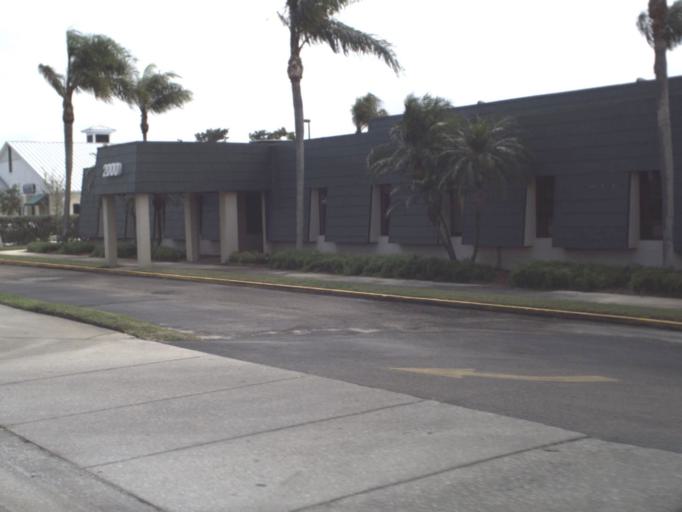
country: US
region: Florida
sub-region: Brevard County
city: Indian Harbour Beach
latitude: 28.1482
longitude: -80.5994
